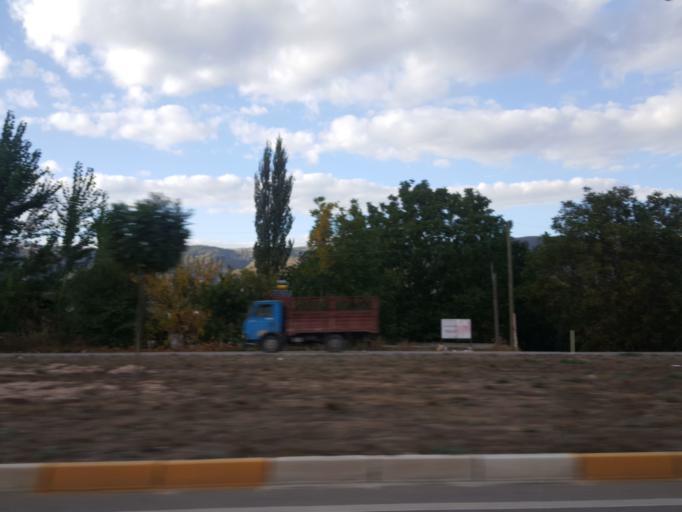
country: TR
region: Tokat
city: Tokat
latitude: 40.3341
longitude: 36.4748
